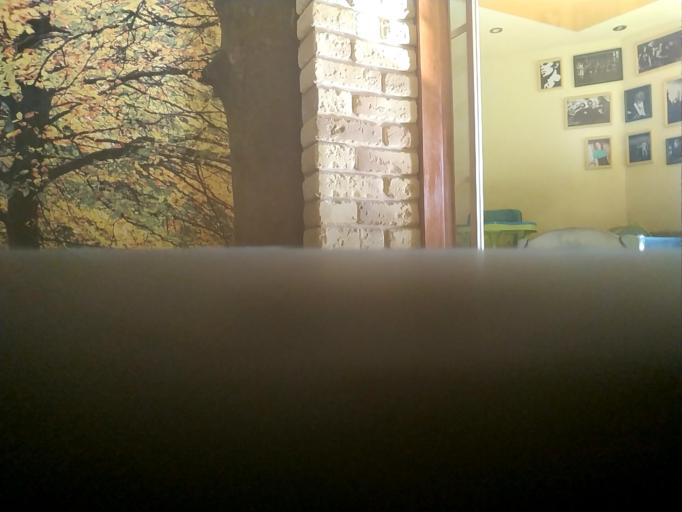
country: RU
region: Smolensk
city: Temkino
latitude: 54.9627
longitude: 34.9518
